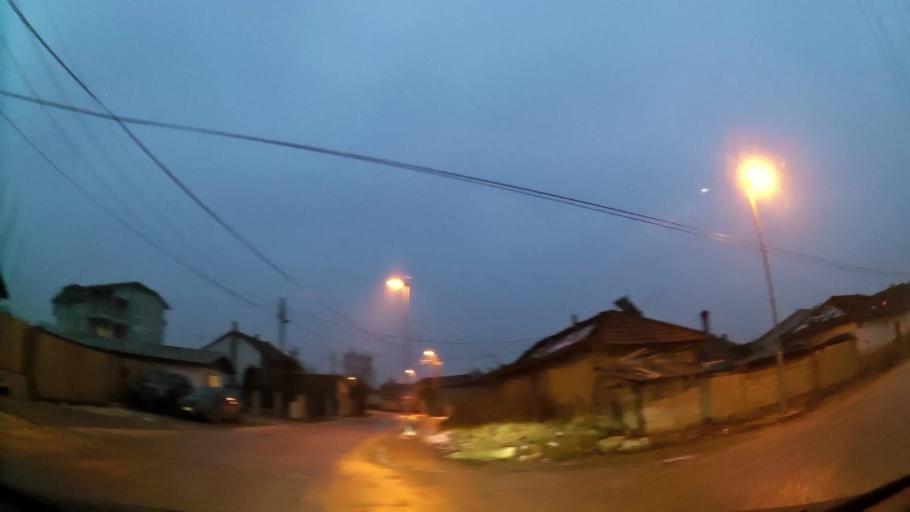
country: MK
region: Kisela Voda
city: Kisela Voda
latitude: 41.9674
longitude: 21.4852
